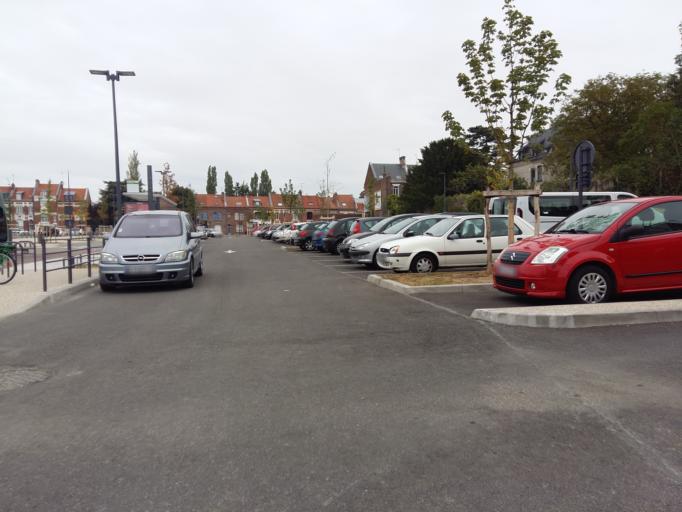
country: FR
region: Picardie
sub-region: Departement de la Somme
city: Amiens
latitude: 49.8782
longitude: 2.2967
